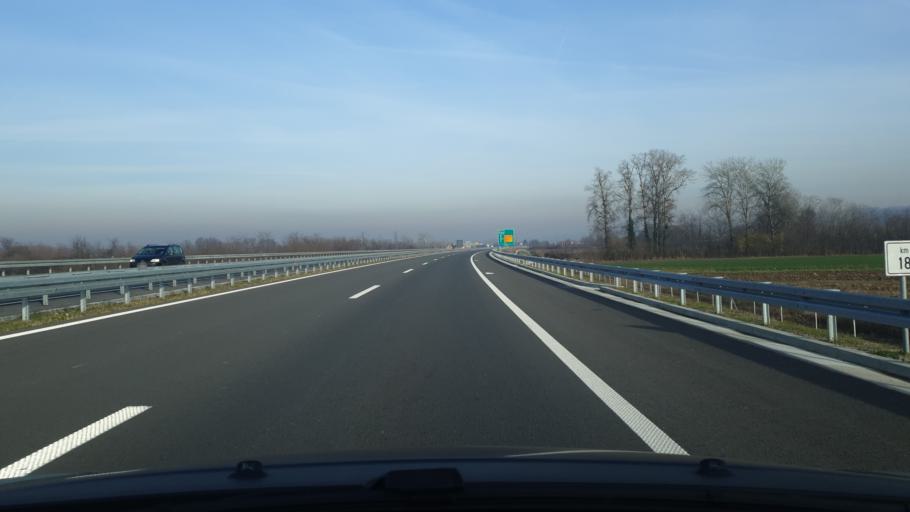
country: RS
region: Central Serbia
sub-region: Belgrade
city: Obrenovac
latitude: 44.6443
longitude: 20.2143
